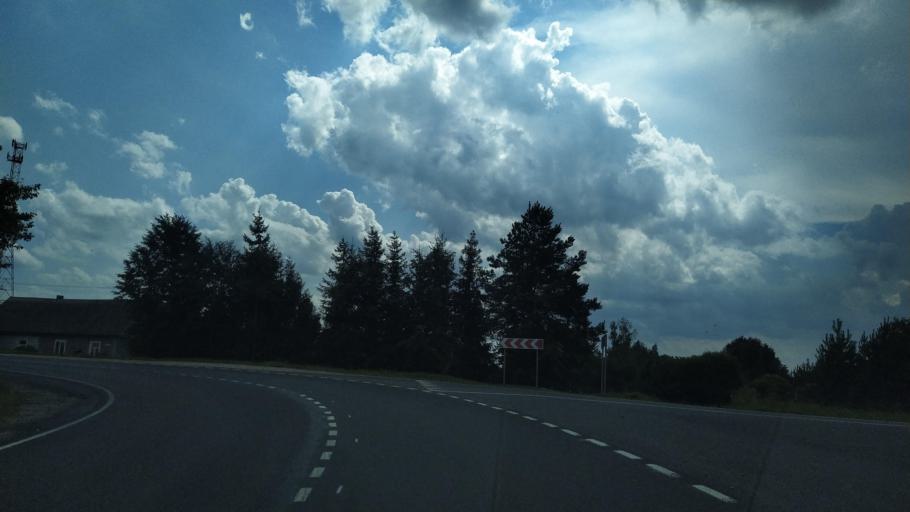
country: RU
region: Pskov
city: Pskov
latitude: 57.7562
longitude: 28.7714
